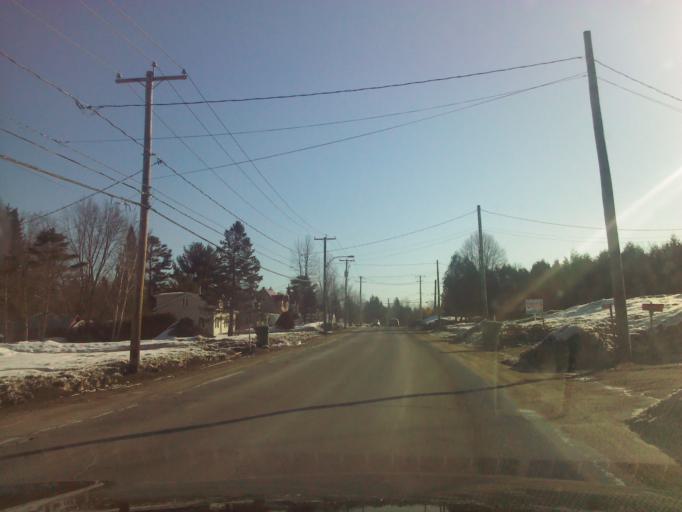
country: CA
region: Quebec
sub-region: Capitale-Nationale
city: Sainte Catherine de la Jacques Cartier
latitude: 46.8460
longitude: -71.6056
